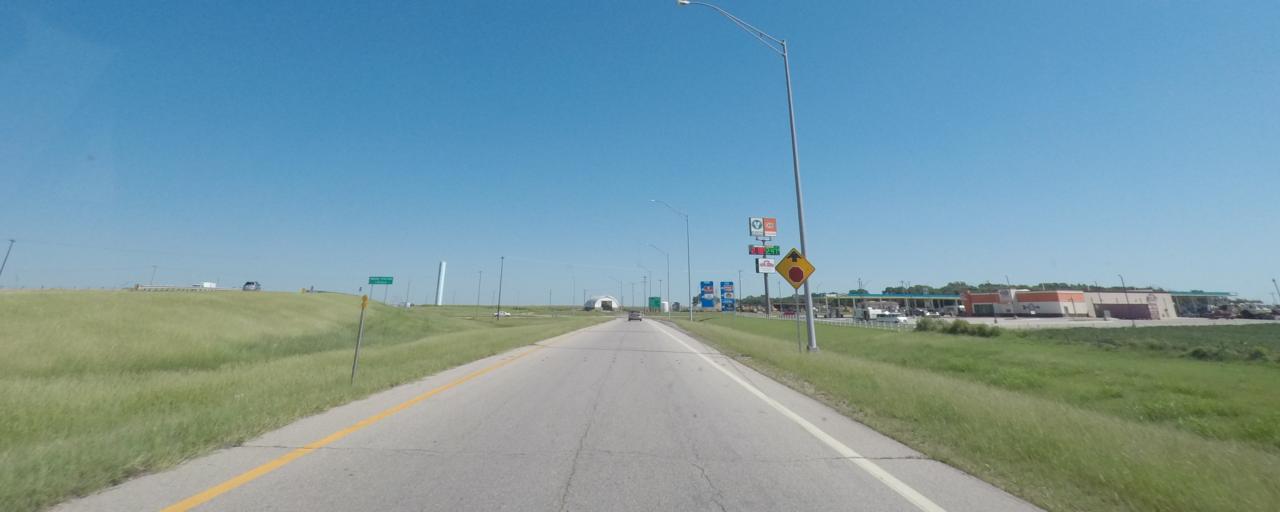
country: US
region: Oklahoma
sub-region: Kay County
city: Tonkawa
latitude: 36.6931
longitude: -97.3455
